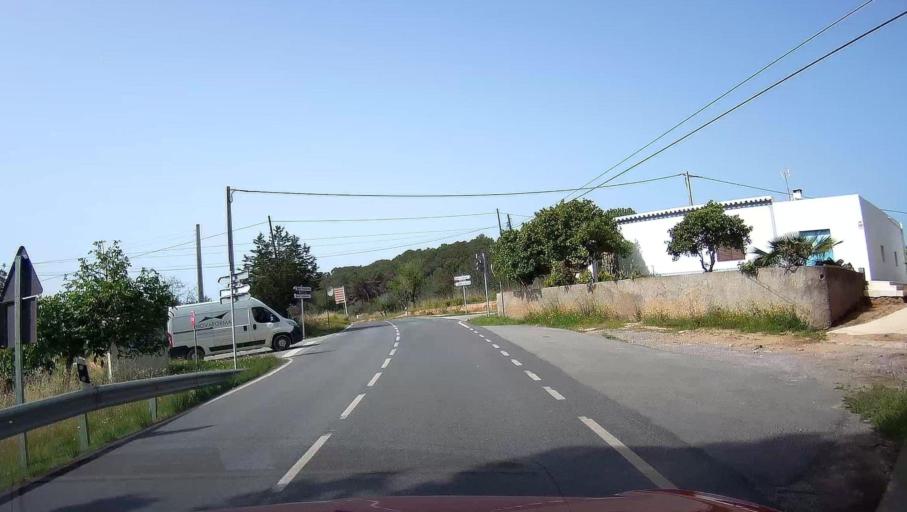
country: ES
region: Balearic Islands
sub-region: Illes Balears
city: Sant Joan de Labritja
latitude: 39.0463
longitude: 1.5696
